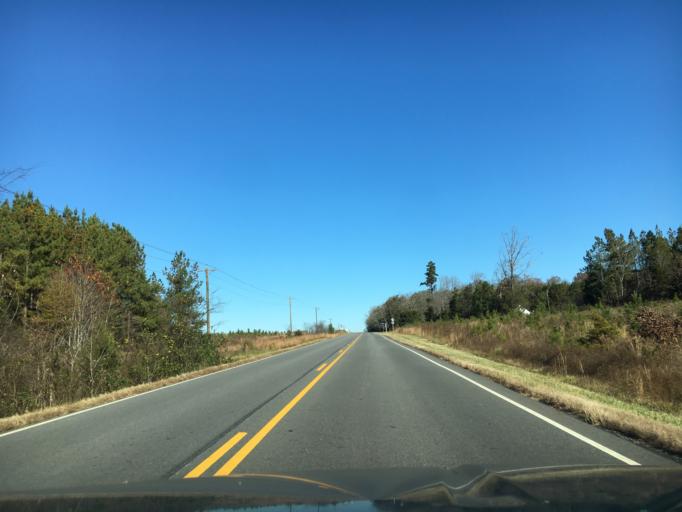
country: US
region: Virginia
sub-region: Buckingham County
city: Buckingham
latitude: 37.5268
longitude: -78.6165
